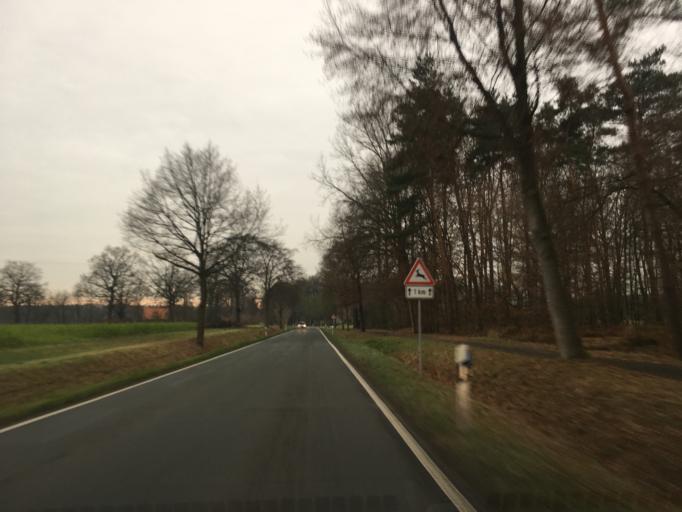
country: DE
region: North Rhine-Westphalia
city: Ludinghausen
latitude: 51.7414
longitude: 7.4492
